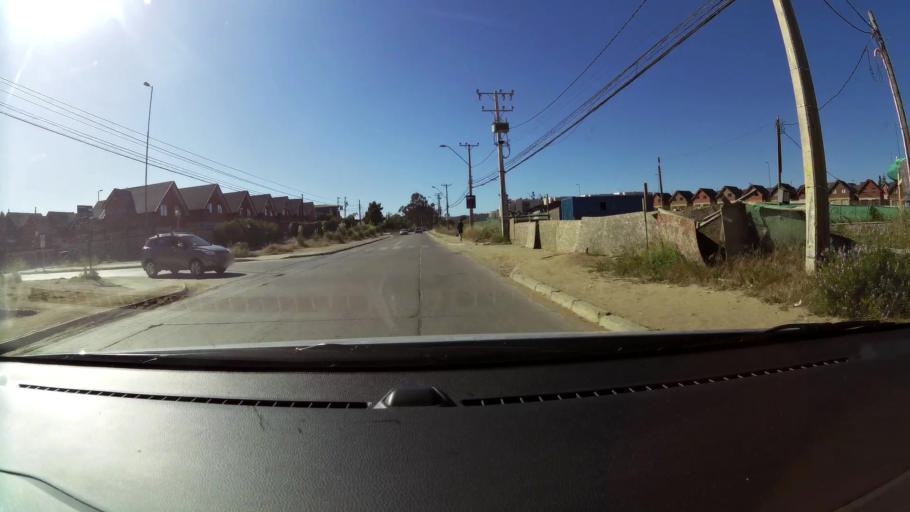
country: CL
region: Valparaiso
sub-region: Provincia de Valparaiso
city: Vina del Mar
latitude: -33.1275
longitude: -71.5695
